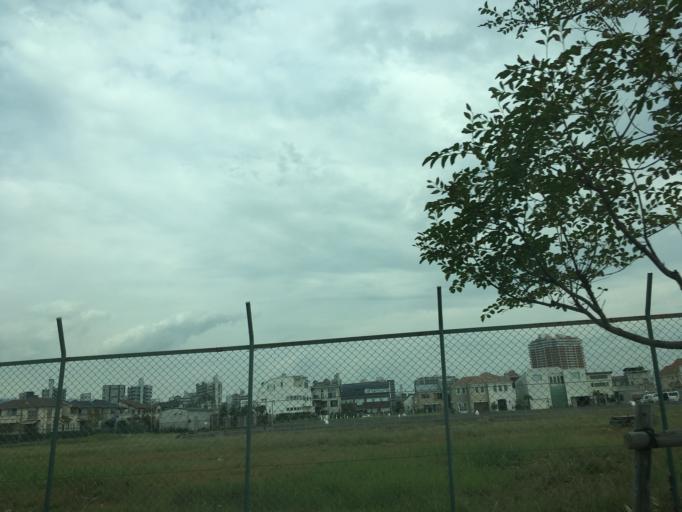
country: JP
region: Hyogo
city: Nishinomiya-hama
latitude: 34.7079
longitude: 135.3156
